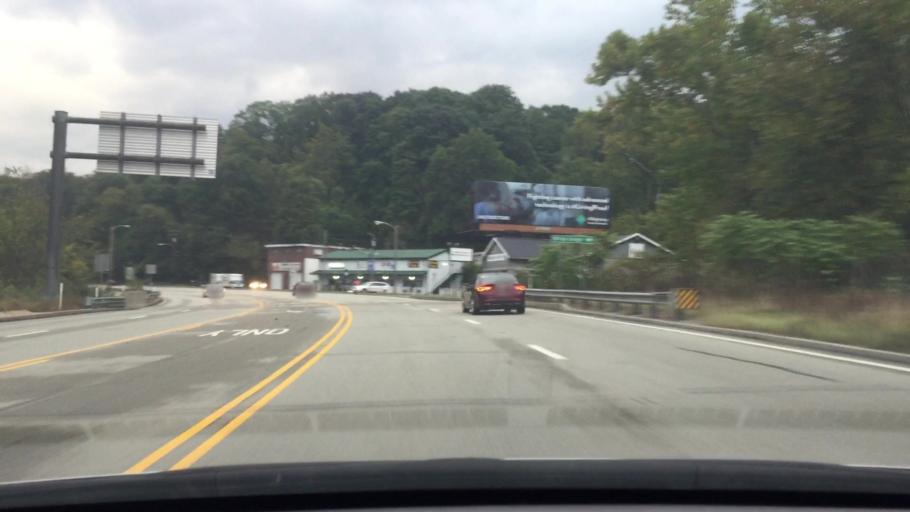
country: US
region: Pennsylvania
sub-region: Allegheny County
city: Jefferson Hills
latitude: 40.2999
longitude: -79.9218
